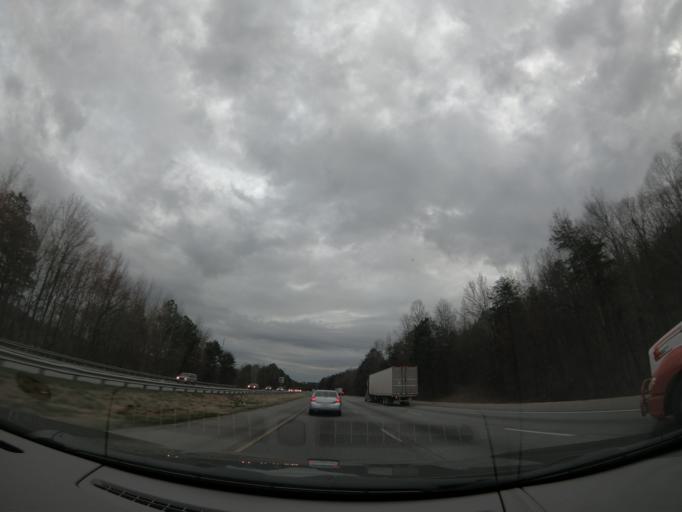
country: US
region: Georgia
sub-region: Whitfield County
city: Dalton
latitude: 34.7463
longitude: -85.0028
